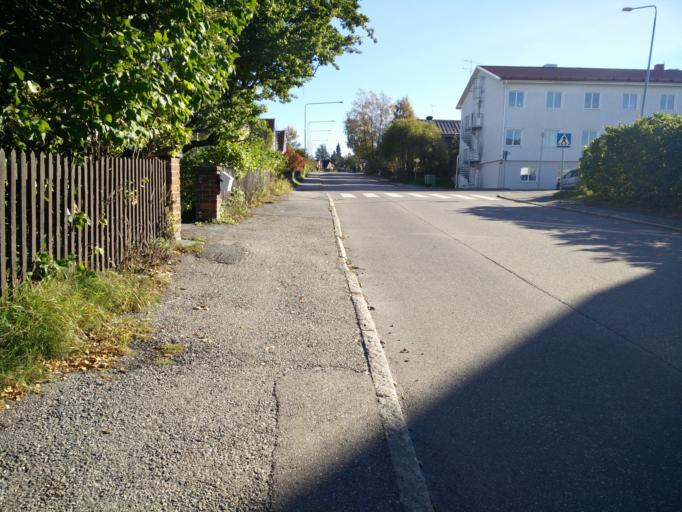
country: SE
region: Vaesternorrland
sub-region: Haernoesands Kommun
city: Haernoesand
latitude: 62.6396
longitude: 17.9560
